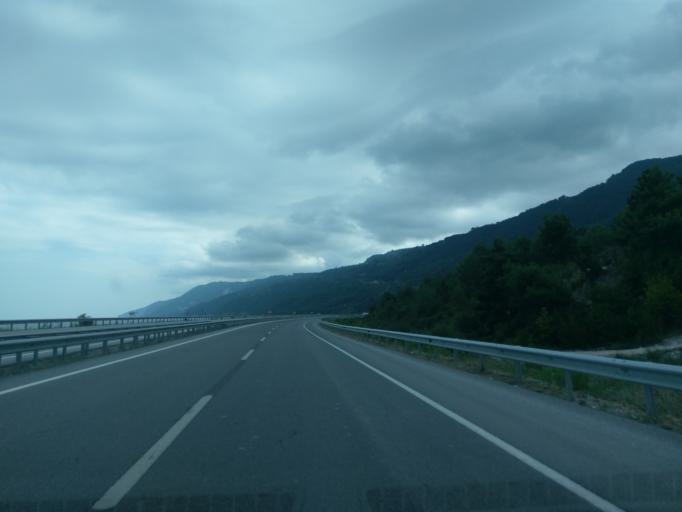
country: TR
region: Sinop
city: Dikmen
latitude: 41.7216
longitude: 35.2694
